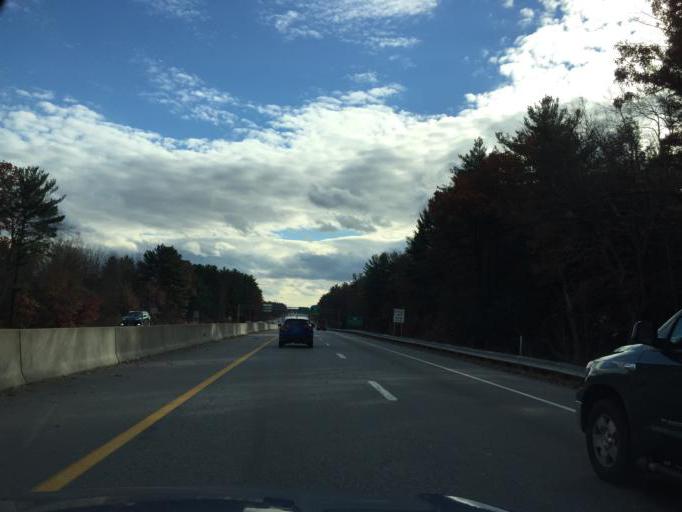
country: US
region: New Hampshire
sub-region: Hillsborough County
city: Bedford
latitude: 42.9390
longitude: -71.4695
